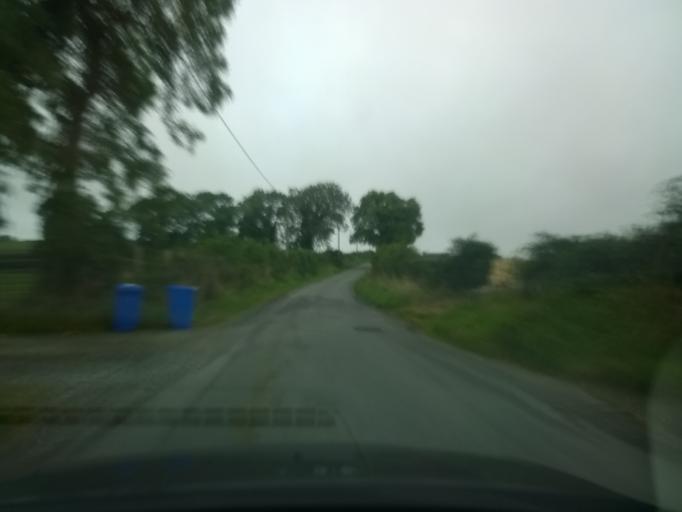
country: IE
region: Leinster
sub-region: Kildare
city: Cherryville
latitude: 53.1781
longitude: -6.9414
